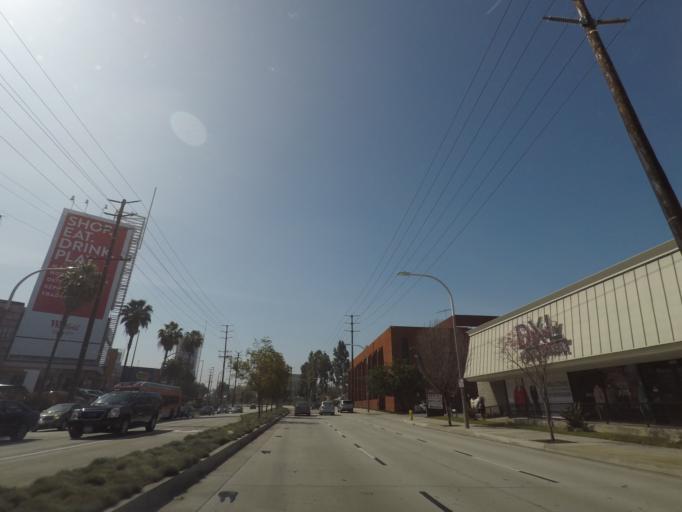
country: US
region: California
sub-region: Los Angeles County
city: Ladera Heights
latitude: 33.9864
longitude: -118.3958
